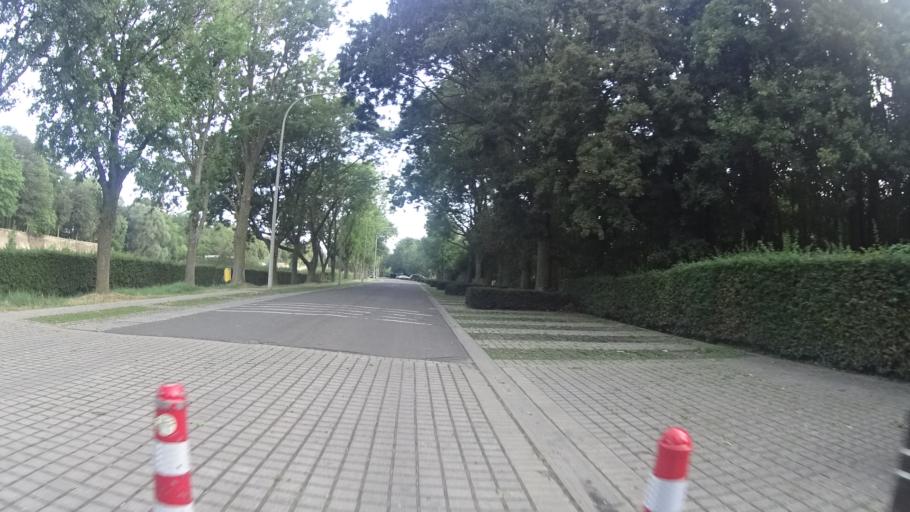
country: BE
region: Flanders
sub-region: Provincie West-Vlaanderen
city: Ieper
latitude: 50.8465
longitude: 2.8935
